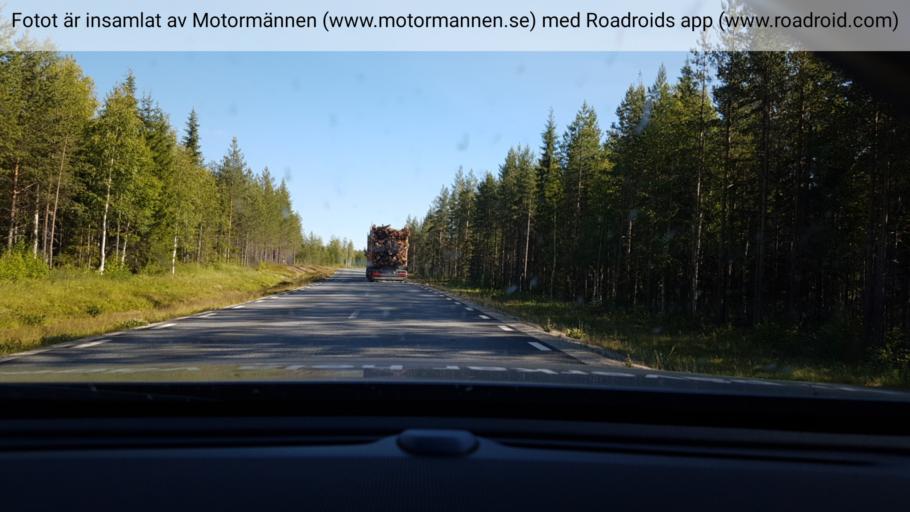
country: SE
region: Vaesterbotten
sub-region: Bjurholms Kommun
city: Bjurholm
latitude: 64.3176
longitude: 19.1591
